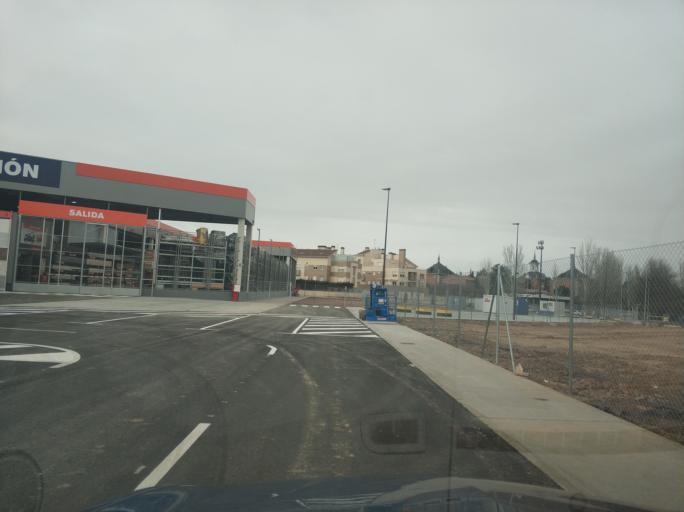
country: ES
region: Castille and Leon
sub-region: Provincia de Salamanca
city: Carbajosa de la Sagrada
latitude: 40.9473
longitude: -5.6440
